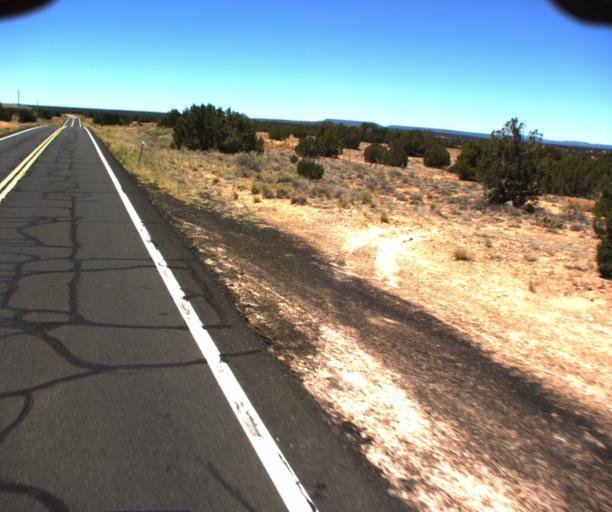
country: US
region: Arizona
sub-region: Coconino County
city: LeChee
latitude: 34.8350
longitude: -110.9463
